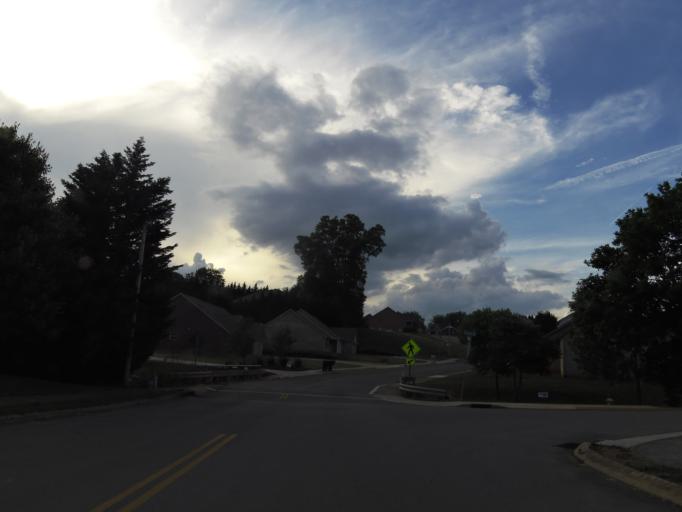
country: US
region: Tennessee
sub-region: Blount County
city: Maryville
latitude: 35.7573
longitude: -83.9469
